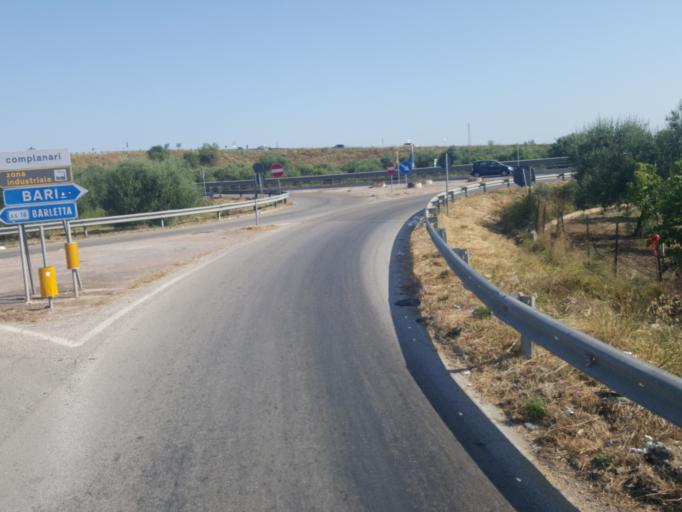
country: IT
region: Apulia
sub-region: Provincia di Barletta - Andria - Trani
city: Barletta
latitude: 41.3018
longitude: 16.3108
